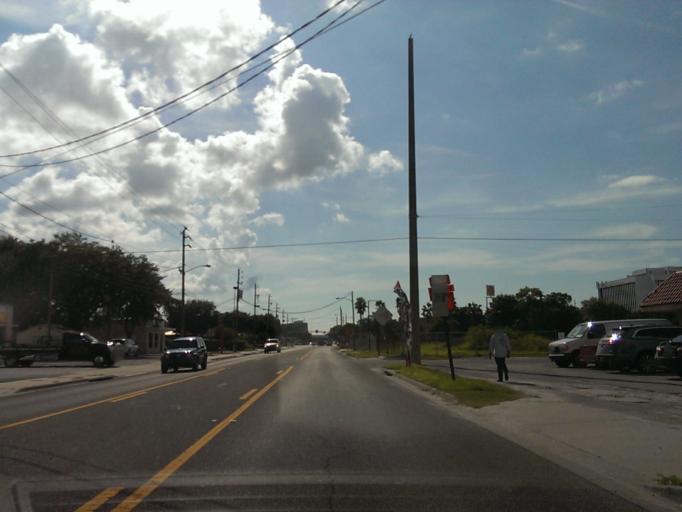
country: US
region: Florida
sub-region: Hillsborough County
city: Tampa
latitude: 27.9522
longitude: -82.5023
